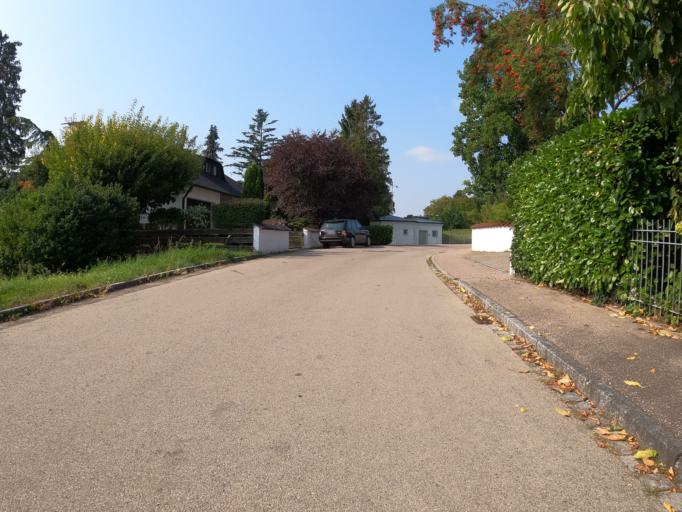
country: DE
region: Bavaria
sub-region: Swabia
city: Guenzburg
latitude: 48.4632
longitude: 10.3094
